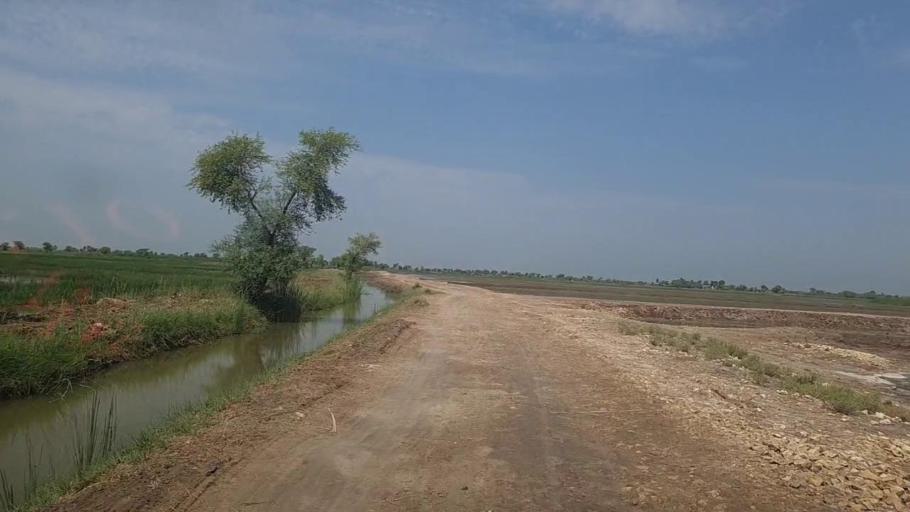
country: PK
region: Sindh
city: Thul
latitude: 28.3006
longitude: 68.6773
